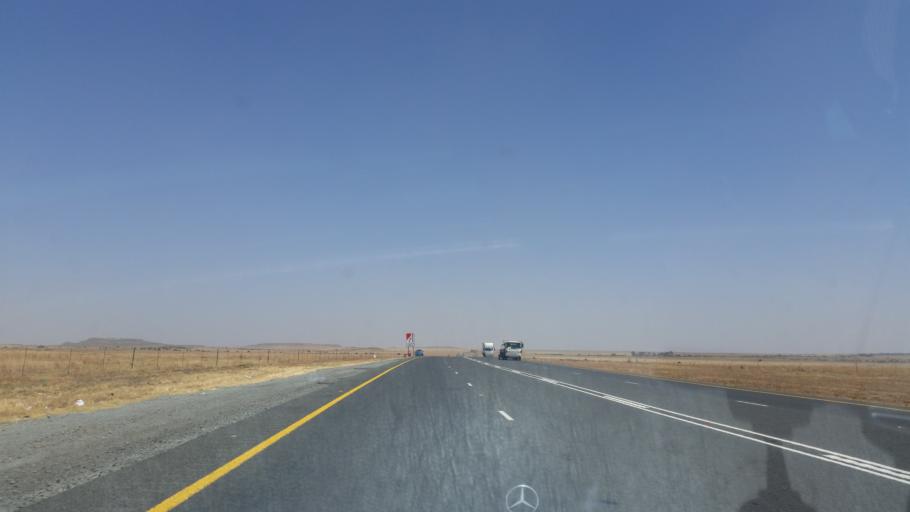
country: ZA
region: Orange Free State
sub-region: Lejweleputswa District Municipality
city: Brandfort
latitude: -28.7674
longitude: 26.7277
